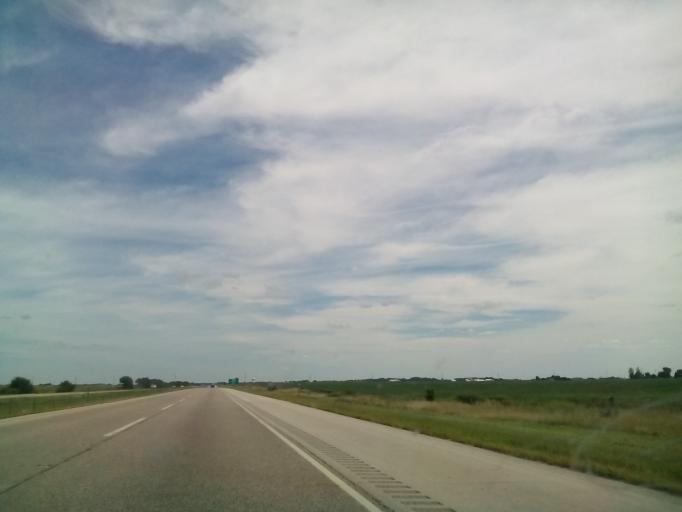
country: US
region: Illinois
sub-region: DeKalb County
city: Malta
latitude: 41.8999
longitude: -88.8240
